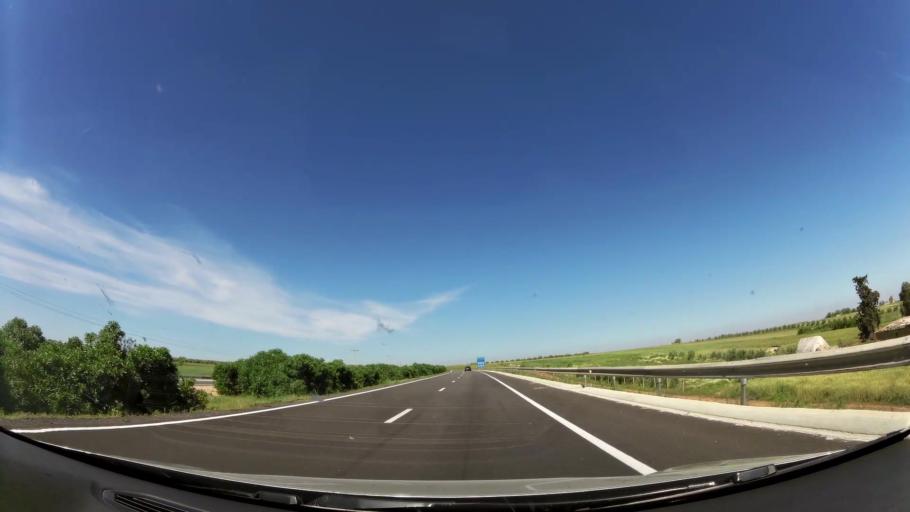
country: MA
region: Meknes-Tafilalet
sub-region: Meknes
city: Meknes
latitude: 33.8332
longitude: -5.4781
